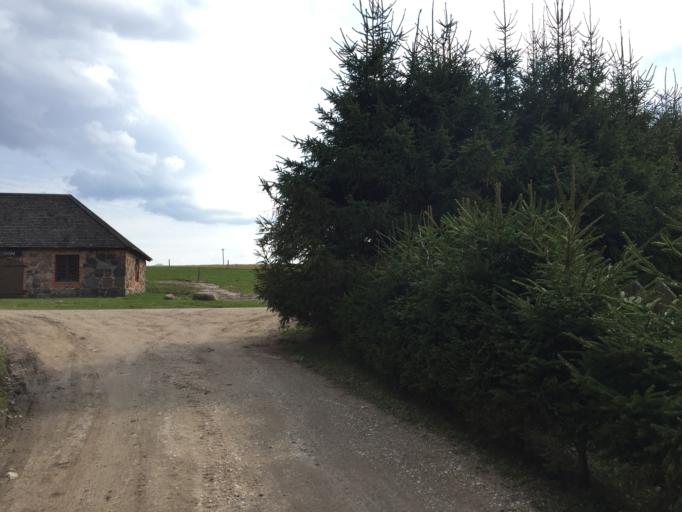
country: RU
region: Pskov
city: Pechory
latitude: 57.7291
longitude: 27.3607
